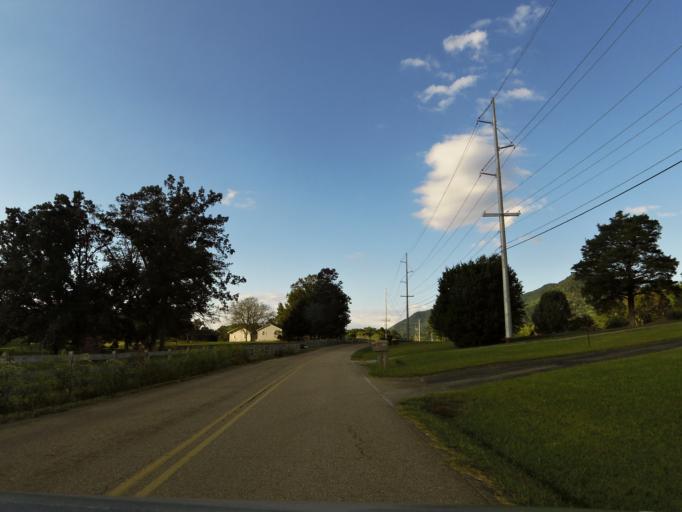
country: US
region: Tennessee
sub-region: Grainger County
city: Blaine
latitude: 36.1501
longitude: -83.7398
